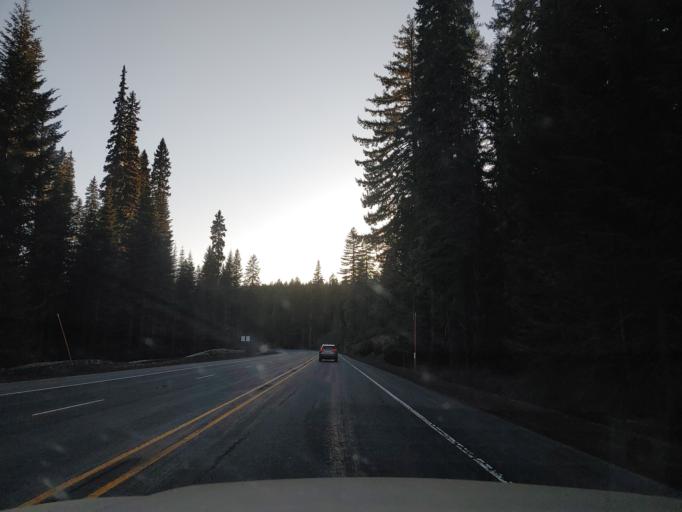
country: US
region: Oregon
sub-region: Lane County
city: Oakridge
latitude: 43.6164
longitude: -122.0976
